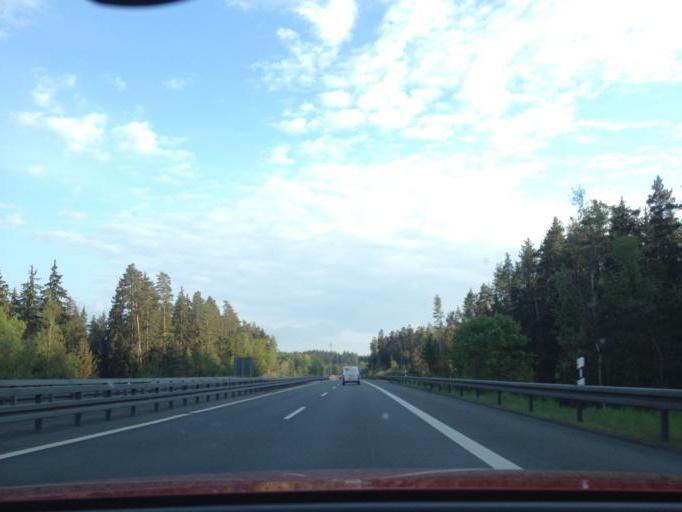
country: DE
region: Bavaria
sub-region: Upper Palatinate
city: Wiesau
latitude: 49.8564
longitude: 12.1794
